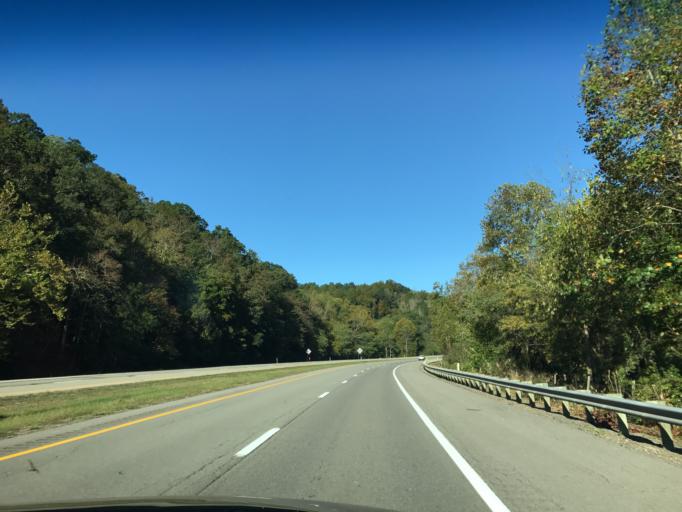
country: US
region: Ohio
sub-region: Washington County
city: Newport
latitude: 39.2477
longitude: -81.2383
